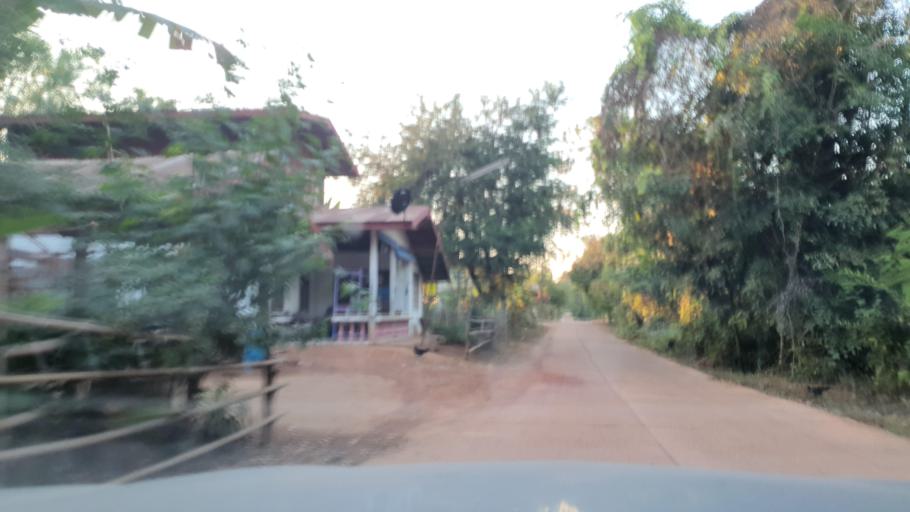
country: TH
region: Nakhon Phanom
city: Ban Phaeng
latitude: 17.8314
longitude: 104.2632
